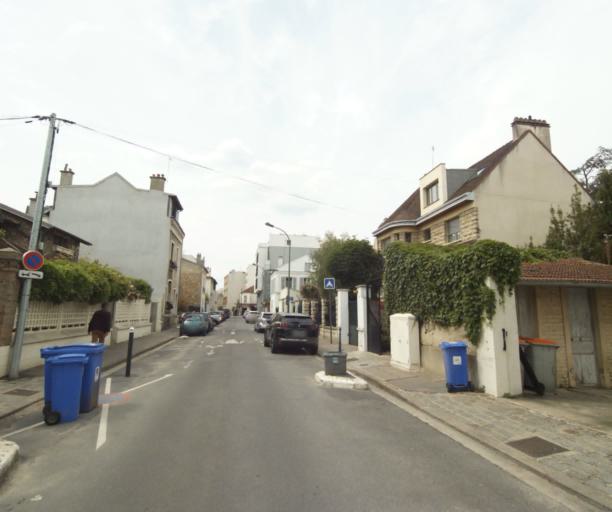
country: FR
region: Ile-de-France
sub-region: Departement des Hauts-de-Seine
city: Asnieres-sur-Seine
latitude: 48.9163
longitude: 2.2789
